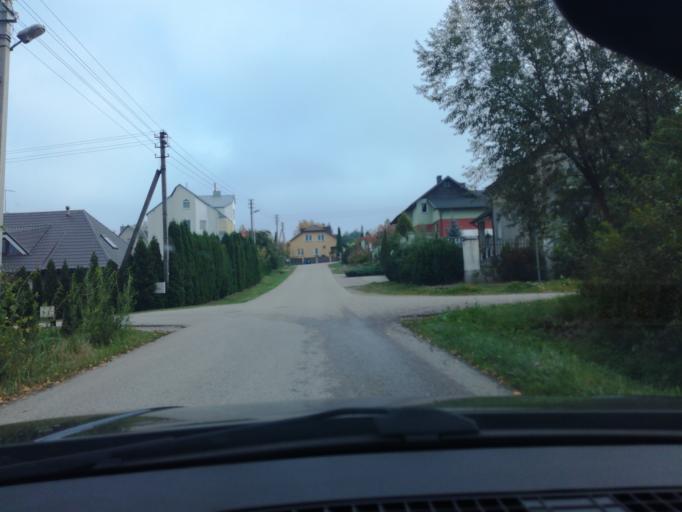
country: LT
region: Alytaus apskritis
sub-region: Alytus
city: Alytus
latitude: 54.3989
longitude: 24.0013
